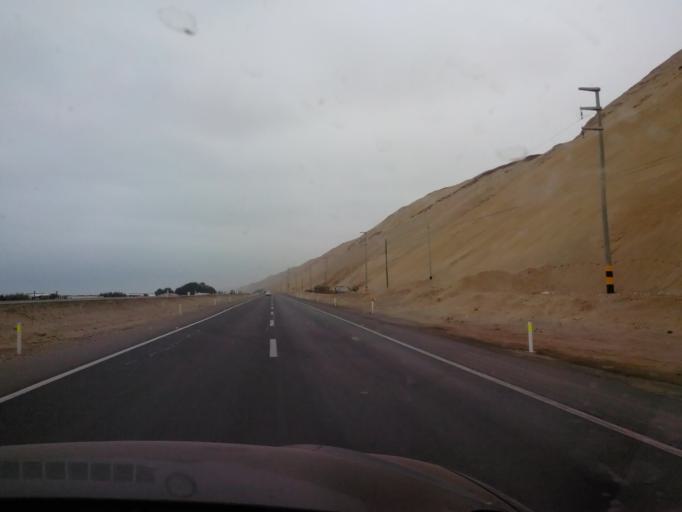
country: PE
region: Ica
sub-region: Provincia de Chincha
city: San Pedro
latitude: -13.3624
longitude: -76.2157
